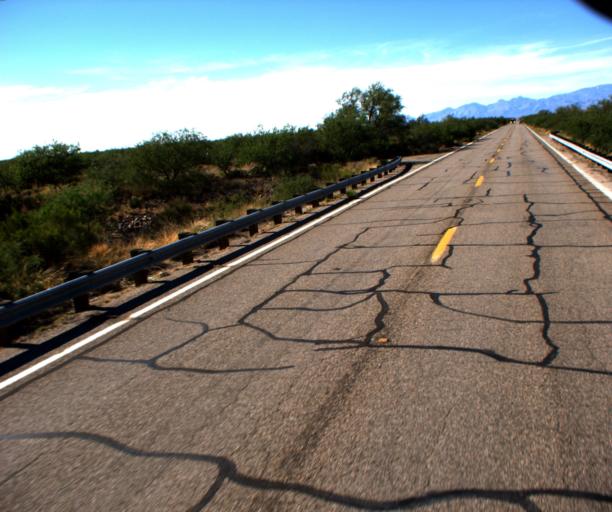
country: US
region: Arizona
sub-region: Pima County
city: Vail
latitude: 31.9521
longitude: -110.6675
